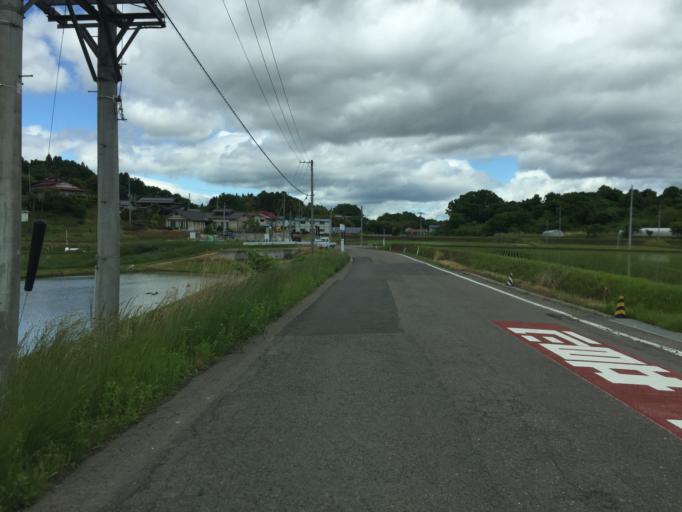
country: JP
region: Fukushima
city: Miharu
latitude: 37.4717
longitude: 140.4600
